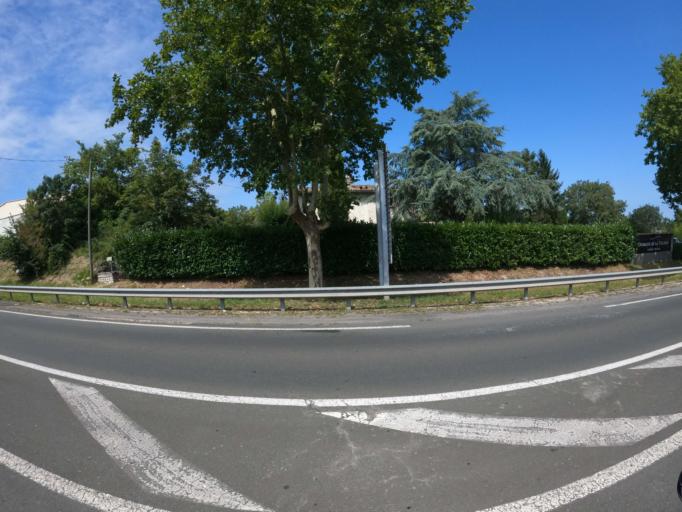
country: FR
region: Poitou-Charentes
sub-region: Departement des Deux-Sevres
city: Bessines
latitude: 46.2980
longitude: -0.4984
